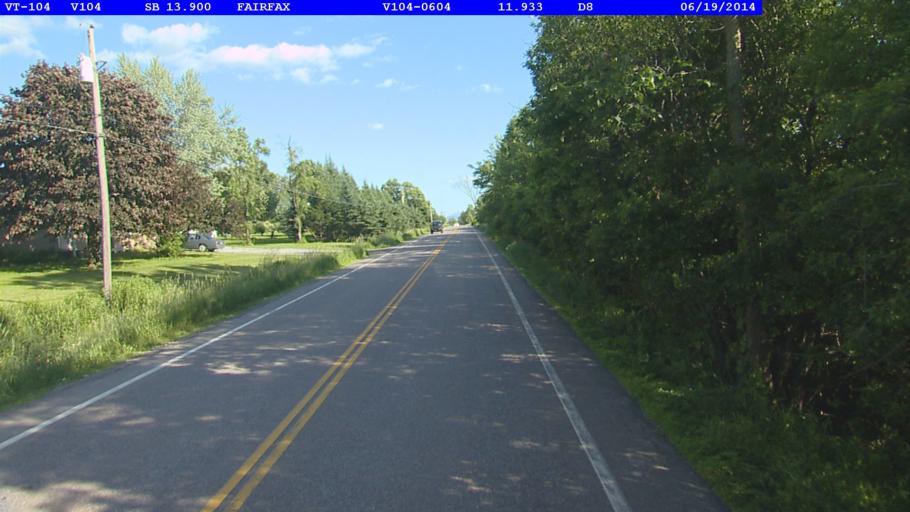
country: US
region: Vermont
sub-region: Franklin County
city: Saint Albans
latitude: 44.7557
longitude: -73.0559
